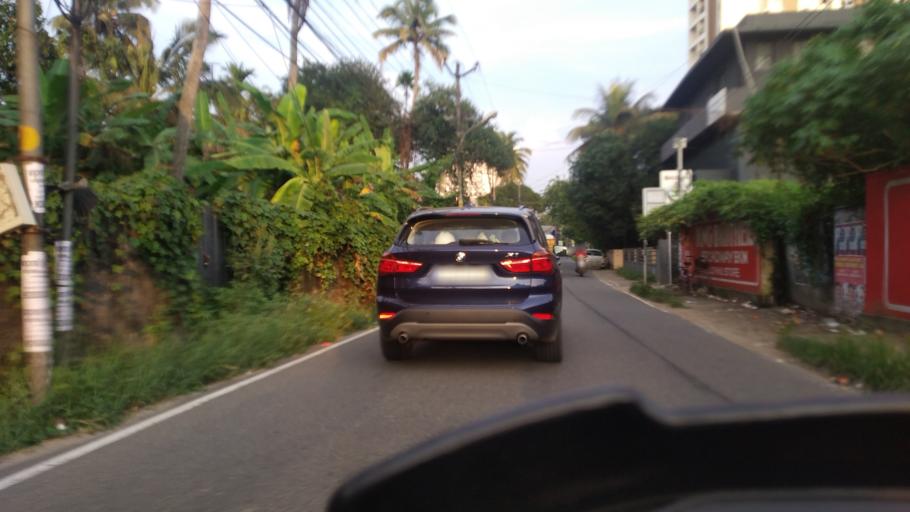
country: IN
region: Kerala
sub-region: Ernakulam
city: Elur
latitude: 10.0197
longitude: 76.2958
